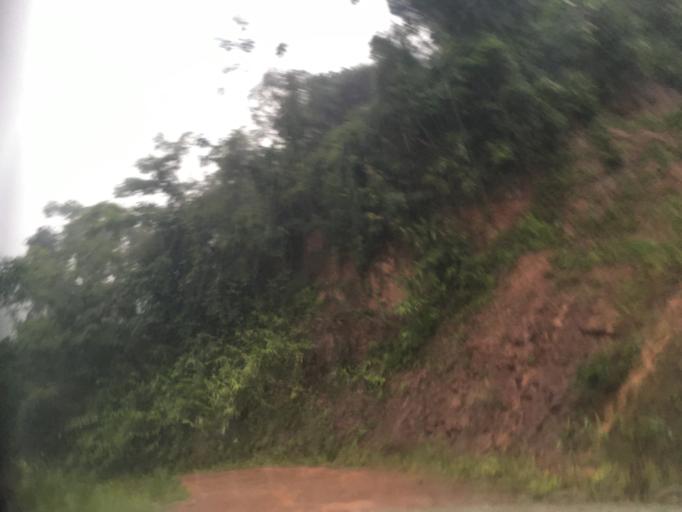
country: LA
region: Oudomxai
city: Muang La
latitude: 21.2315
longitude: 101.9606
